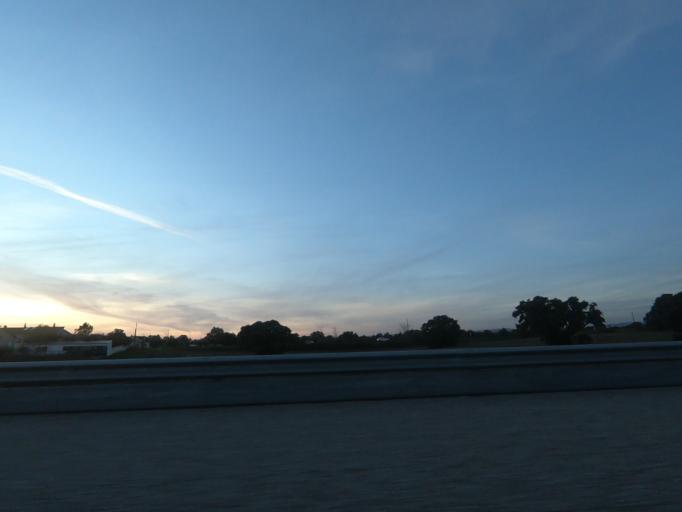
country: PT
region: Santarem
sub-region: Alcanena
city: Alcanena
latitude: 39.4115
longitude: -8.6364
